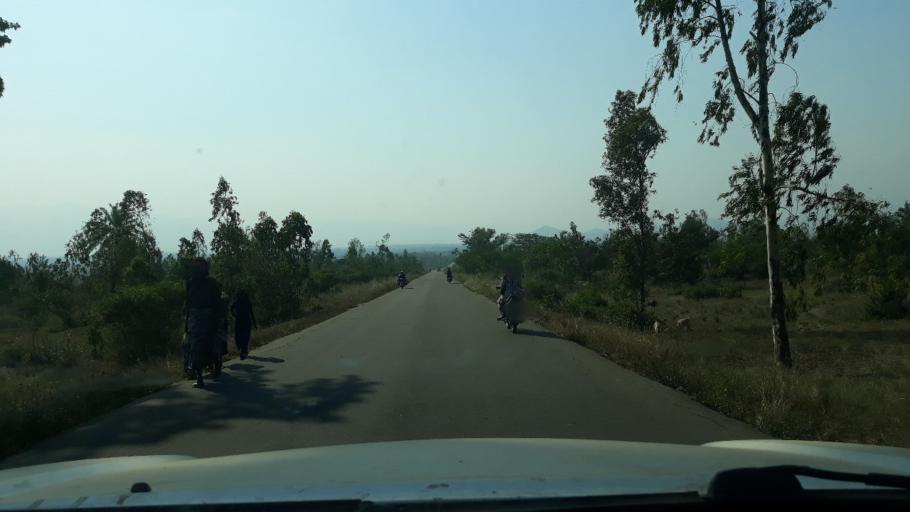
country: BI
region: Cibitoke
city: Cibitoke
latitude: -2.8950
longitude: 29.0487
